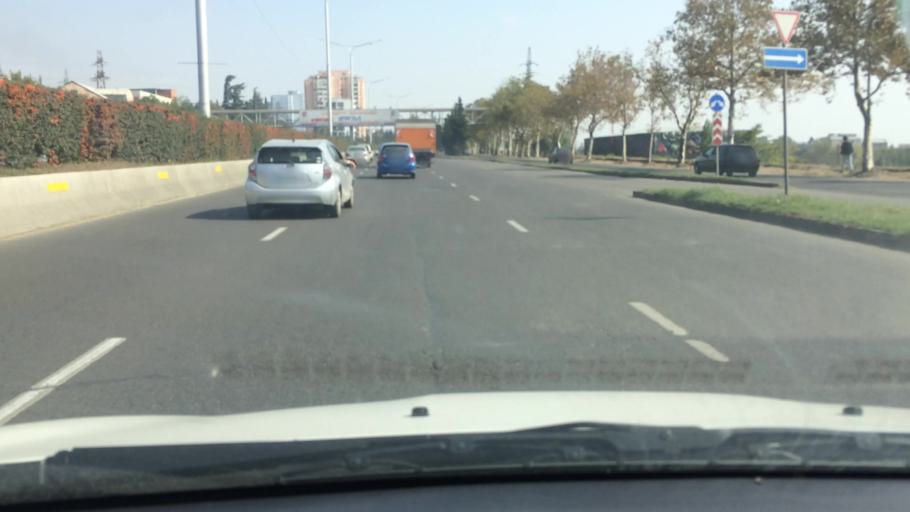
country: GE
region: T'bilisi
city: Tbilisi
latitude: 41.6880
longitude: 44.8472
